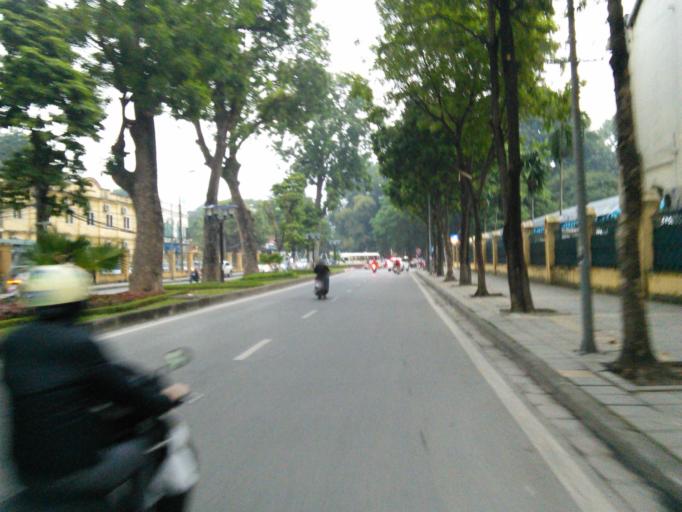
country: VN
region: Ha Noi
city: Hanoi
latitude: 21.0325
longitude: 105.8405
